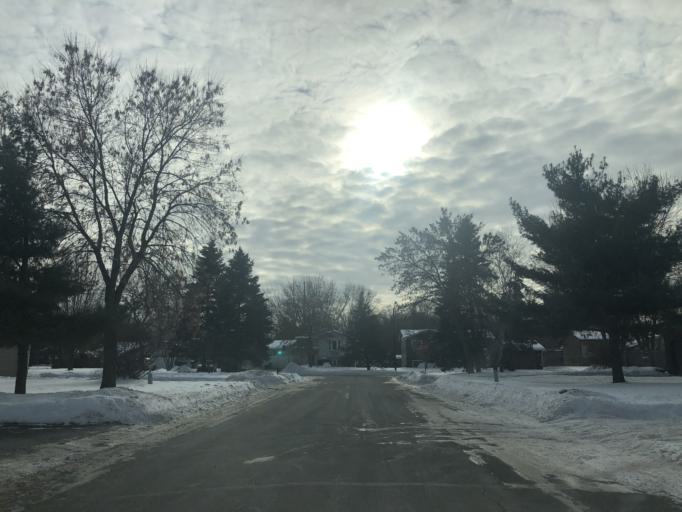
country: US
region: Minnesota
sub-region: Anoka County
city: Circle Pines
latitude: 45.1543
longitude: -93.1613
